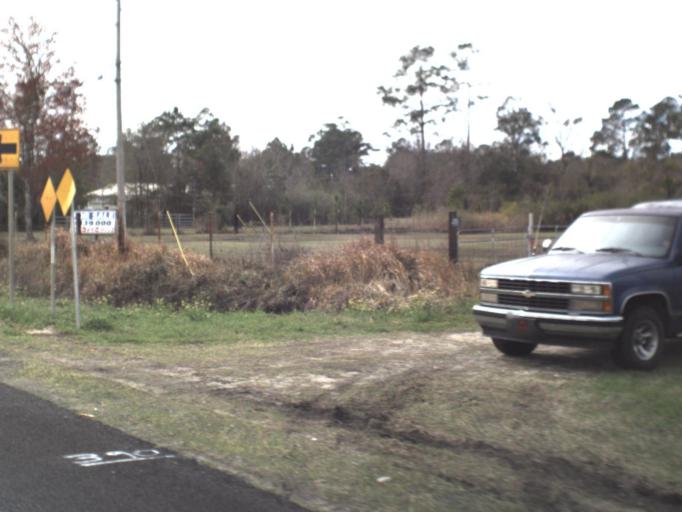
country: US
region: Florida
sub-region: Bay County
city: Youngstown
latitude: 30.3246
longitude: -85.4508
